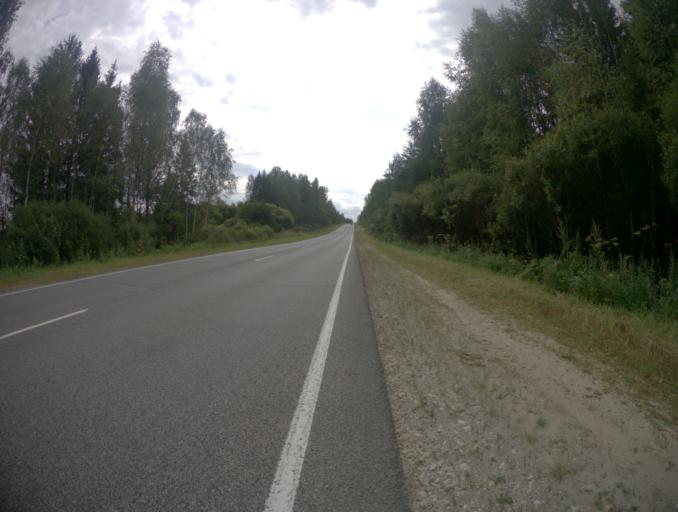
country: RU
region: Vladimir
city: Golovino
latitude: 55.9361
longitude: 40.5927
